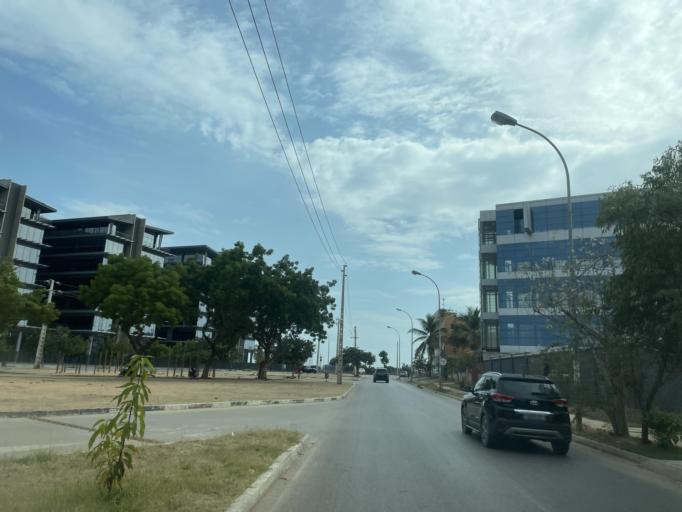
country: AO
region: Luanda
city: Luanda
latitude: -8.9190
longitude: 13.1792
